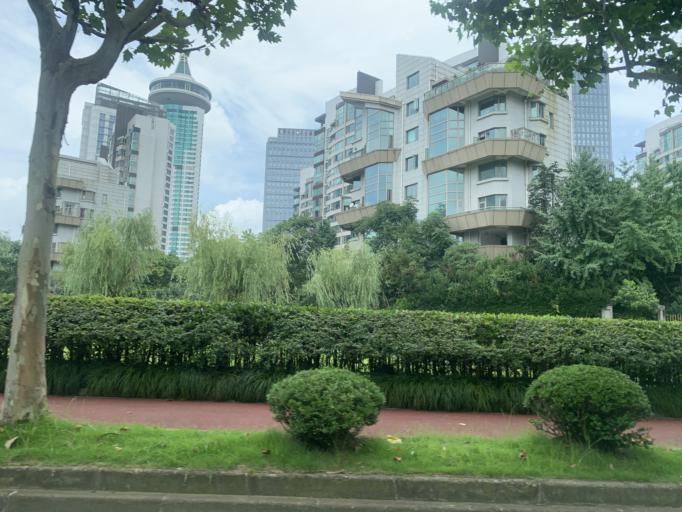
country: CN
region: Shanghai Shi
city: Huamu
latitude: 31.2135
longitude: 121.5338
